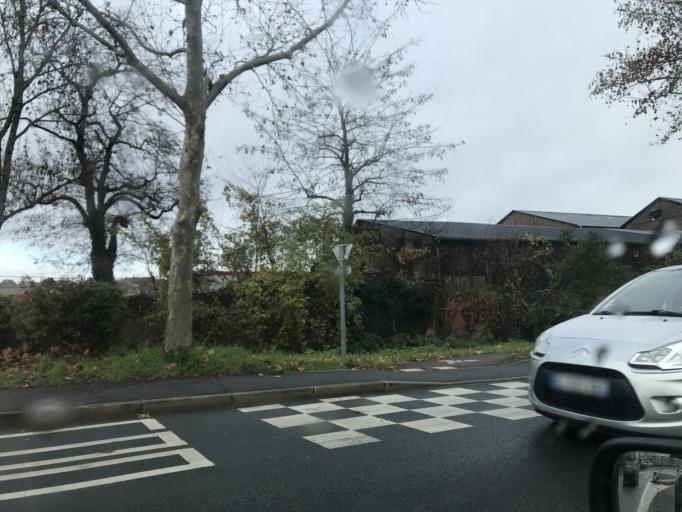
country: FR
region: Ile-de-France
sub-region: Departement du Val-d'Oise
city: Saint-Ouen-l'Aumone
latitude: 49.0525
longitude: 2.1156
